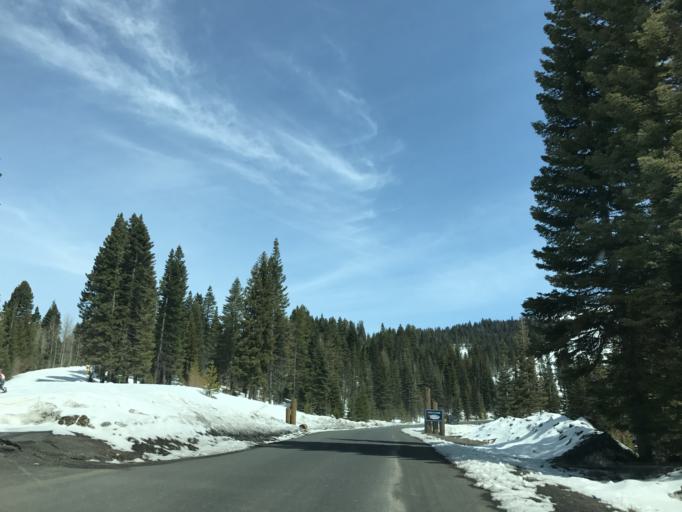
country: US
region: Idaho
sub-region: Valley County
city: McCall
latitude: 45.0013
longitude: -116.1617
